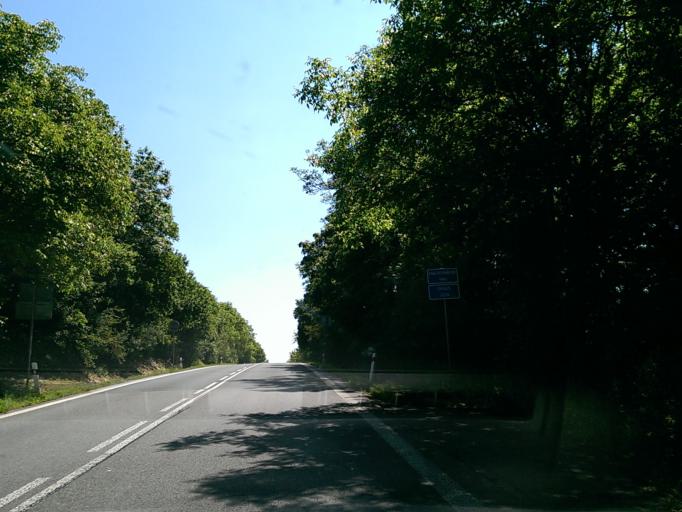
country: CZ
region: Liberecky
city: Rovensko pod Troskami
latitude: 50.5138
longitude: 15.2553
